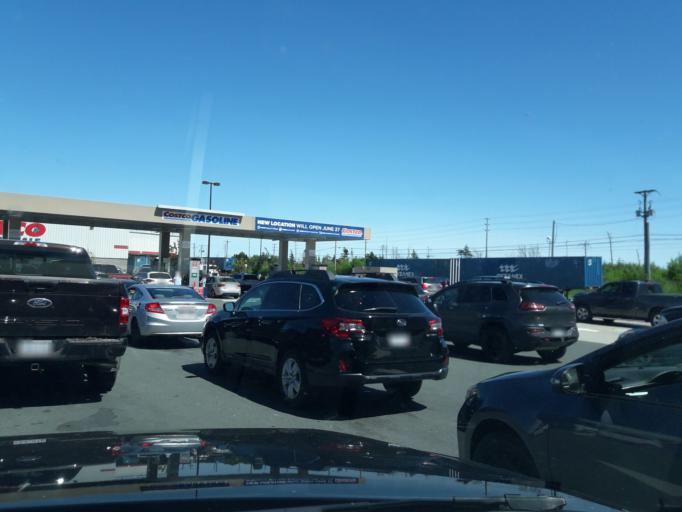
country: CA
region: Newfoundland and Labrador
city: St. John's
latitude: 47.6137
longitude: -52.7154
